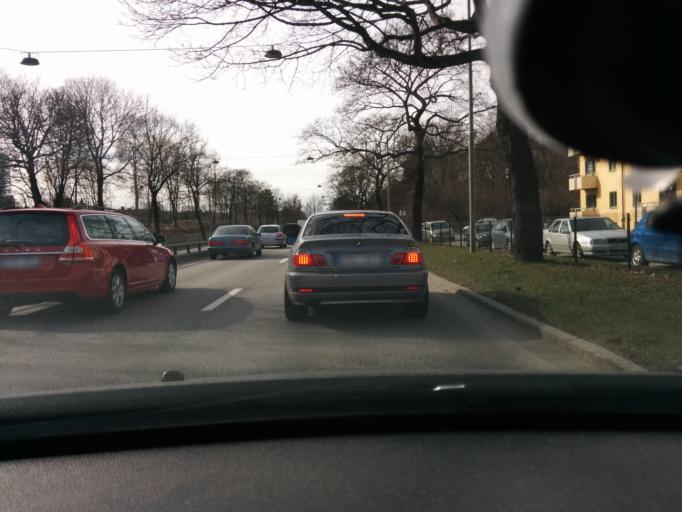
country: SE
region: Stockholm
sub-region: Stockholms Kommun
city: Bromma
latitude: 59.3385
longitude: 17.9466
